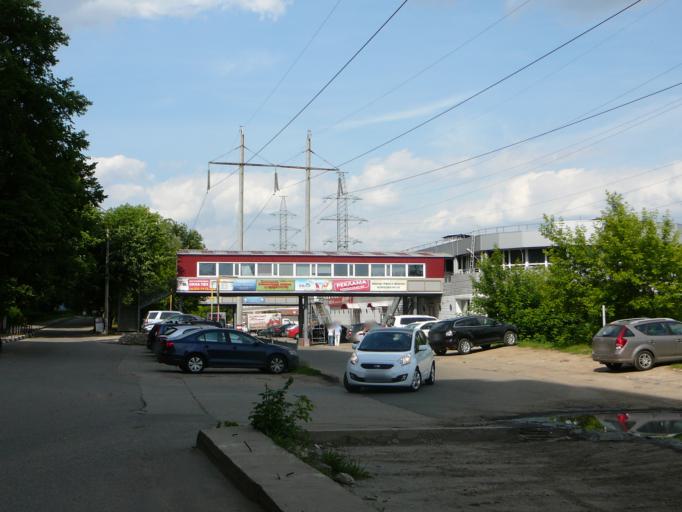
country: RU
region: Moskovskaya
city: Krasnogorsk
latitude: 55.8143
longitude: 37.3226
